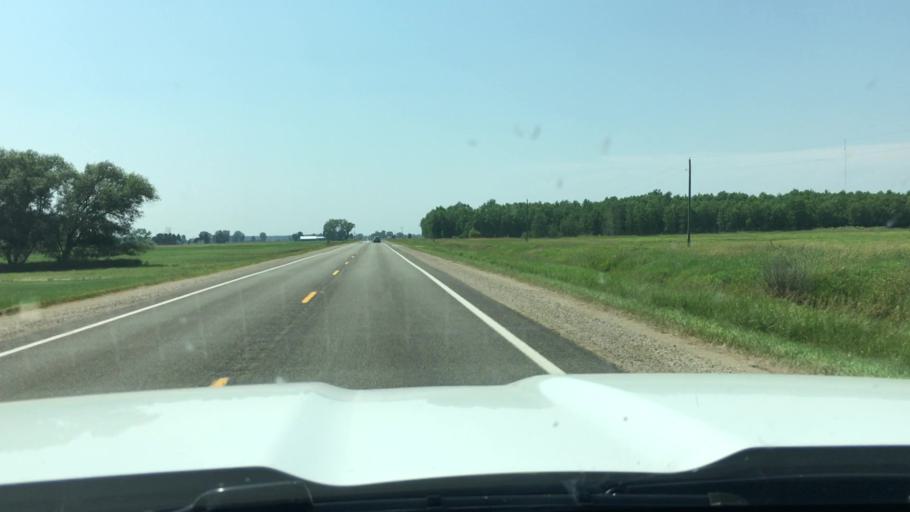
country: US
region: Michigan
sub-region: Clinton County
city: Ovid
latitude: 43.1759
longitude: -84.4345
